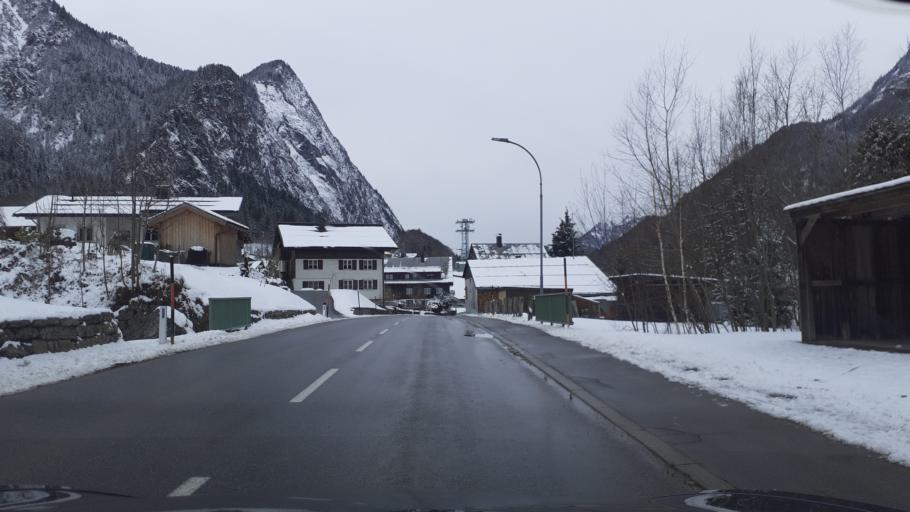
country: AT
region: Vorarlberg
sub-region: Politischer Bezirk Bludenz
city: Dalaas
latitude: 47.1222
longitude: 9.9893
